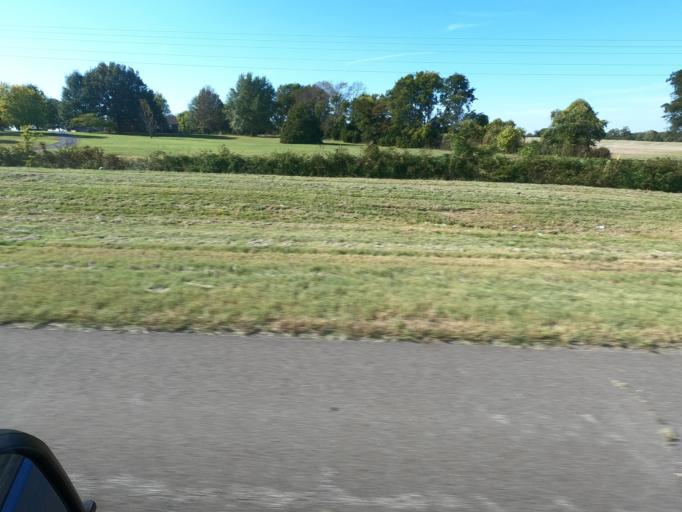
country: US
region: Tennessee
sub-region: Dyer County
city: Newbern
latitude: 36.1137
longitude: -89.2892
